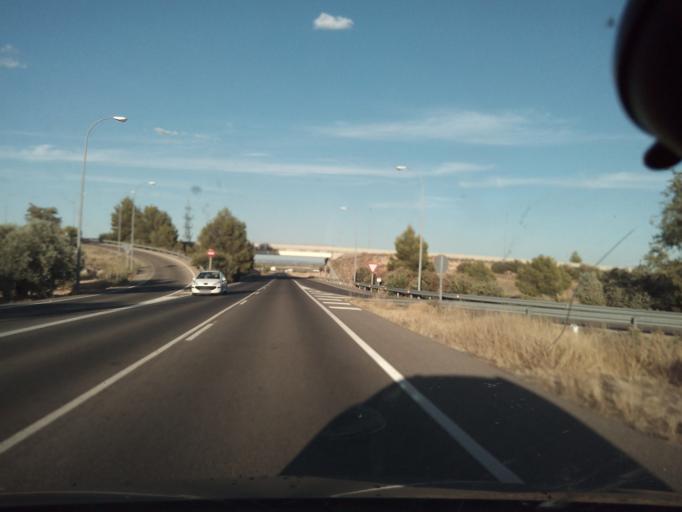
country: ES
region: Castille-La Mancha
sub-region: Province of Toledo
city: Villacanas
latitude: 39.6103
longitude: -3.3578
